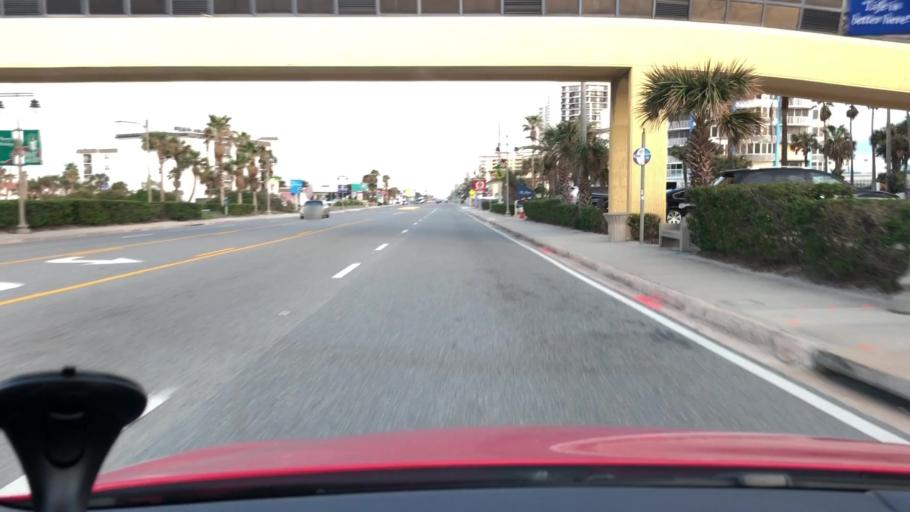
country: US
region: Florida
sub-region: Volusia County
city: Daytona Beach Shores
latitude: 29.1807
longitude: -80.9852
